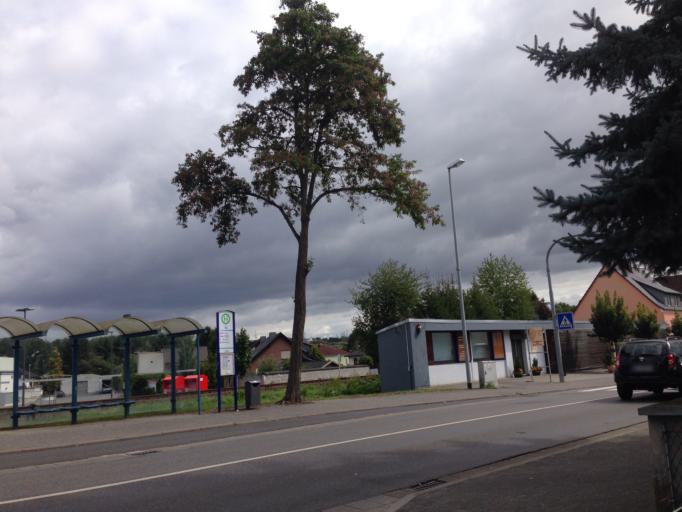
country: DE
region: Hesse
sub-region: Regierungsbezirk Giessen
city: Elz
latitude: 50.4063
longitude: 8.0368
